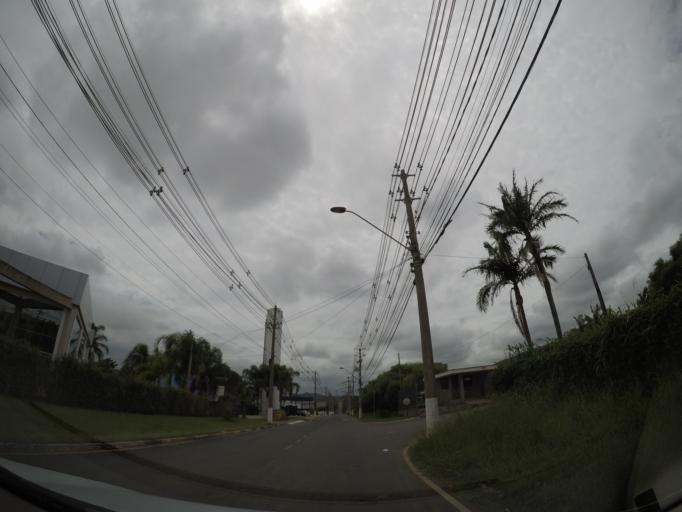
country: BR
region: Sao Paulo
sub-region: Vinhedo
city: Vinhedo
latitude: -23.0695
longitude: -46.9970
